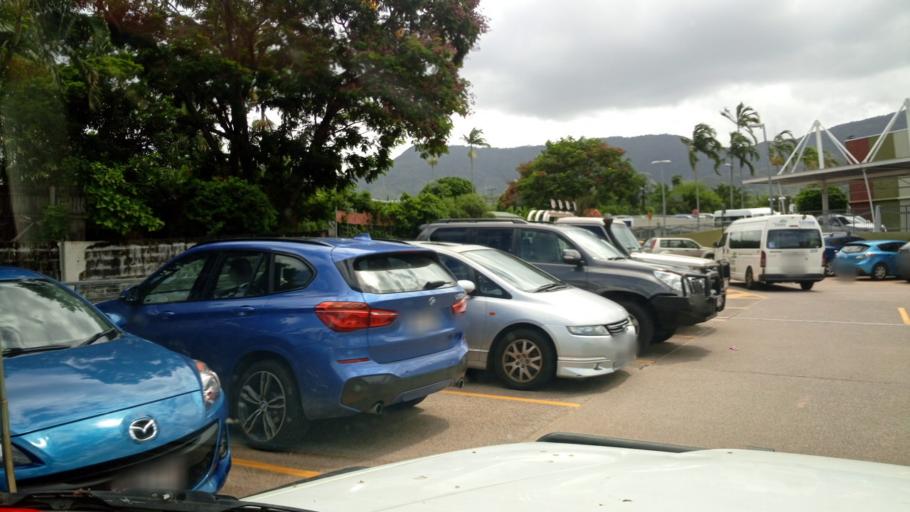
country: AU
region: Queensland
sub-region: Cairns
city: Woree
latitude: -16.9453
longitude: 145.7406
